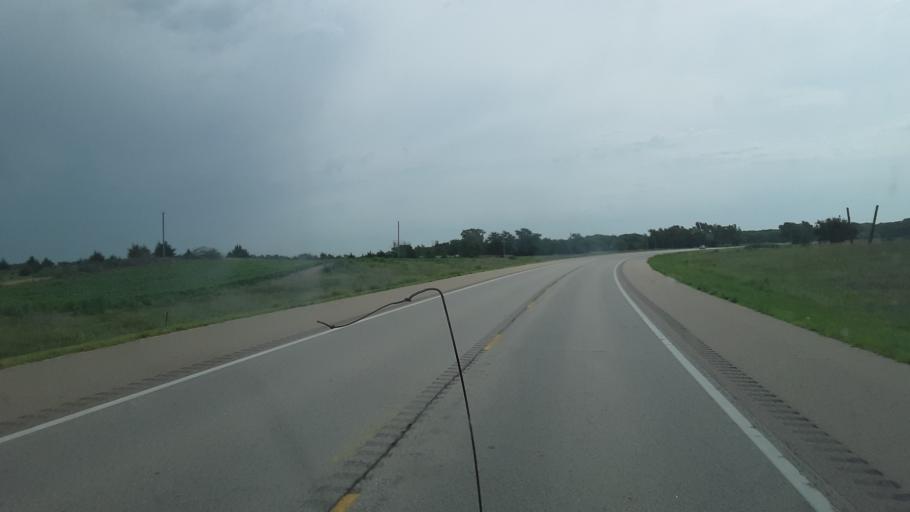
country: US
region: Kansas
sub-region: Stafford County
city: Stafford
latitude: 37.9834
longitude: -98.3868
